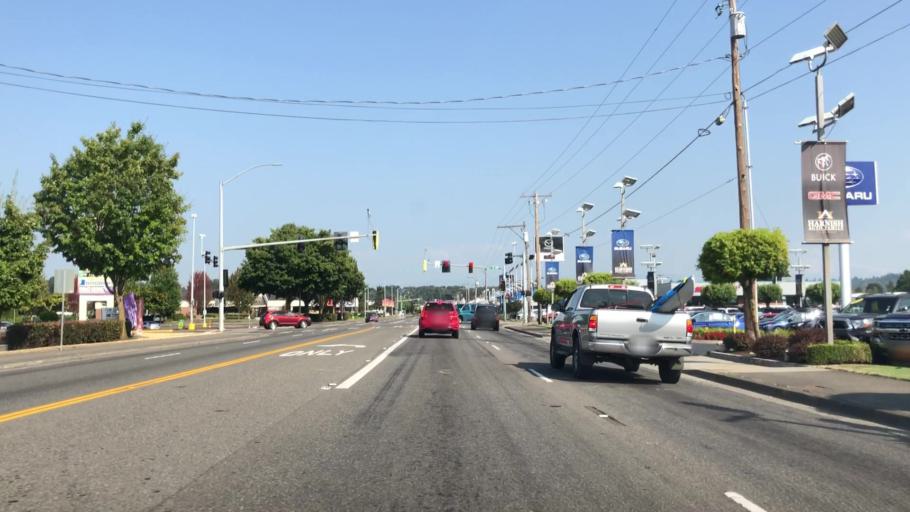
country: US
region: Washington
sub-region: Pierce County
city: Puyallup
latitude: 47.2011
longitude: -122.3030
